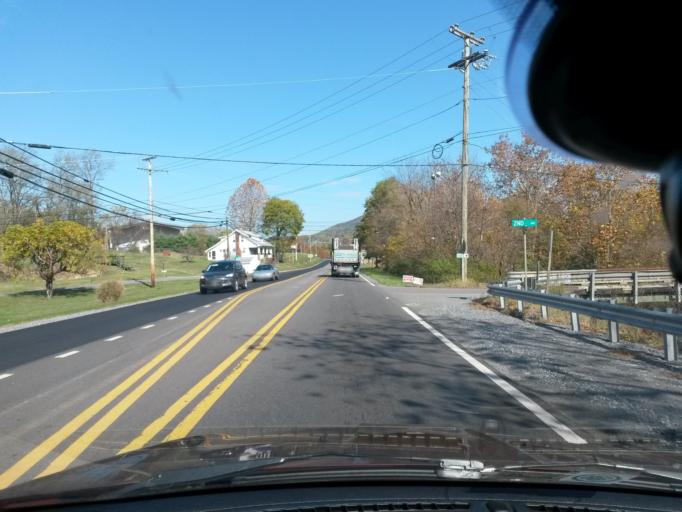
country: US
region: Virginia
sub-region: Botetourt County
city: Cloverdale
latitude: 37.3702
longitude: -79.9078
